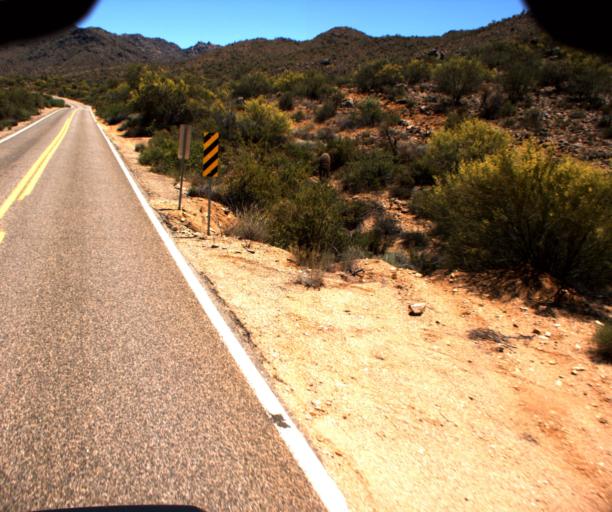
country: US
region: Arizona
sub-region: Yavapai County
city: Bagdad
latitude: 34.4625
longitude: -113.0417
